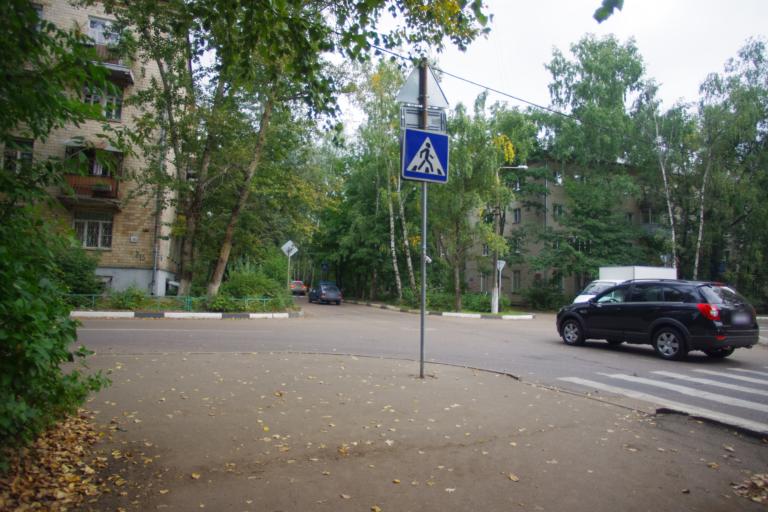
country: RU
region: Moskovskaya
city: Krasnogorsk
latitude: 55.8169
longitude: 37.3339
